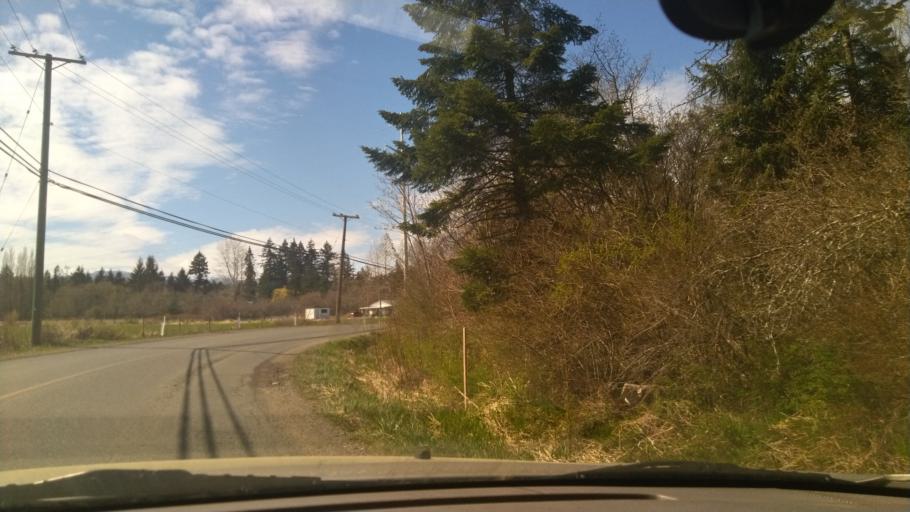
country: CA
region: British Columbia
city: Courtenay
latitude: 49.6956
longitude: -125.0107
